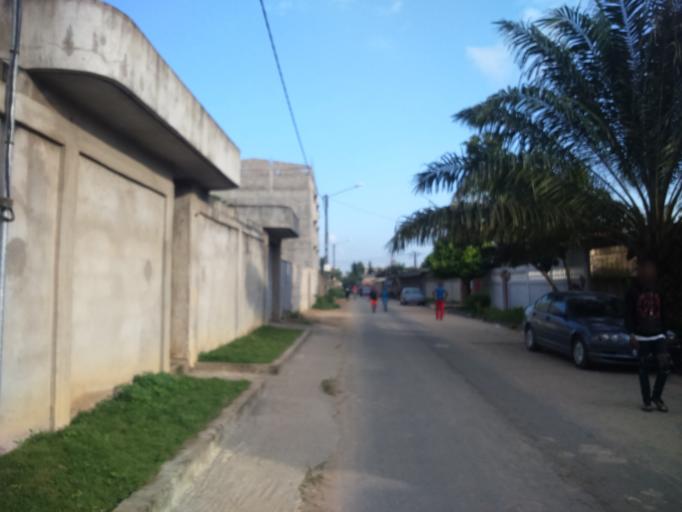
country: CI
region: Lagunes
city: Abobo
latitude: 5.3992
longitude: -3.9789
